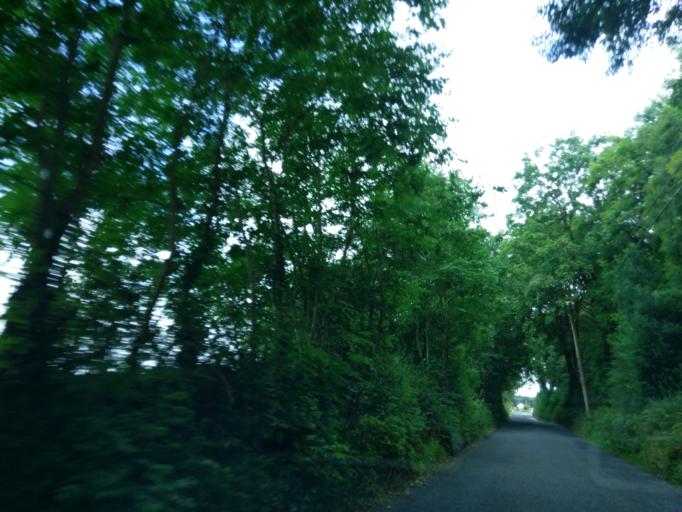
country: IE
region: Connaught
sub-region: County Galway
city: Athenry
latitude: 53.3266
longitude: -8.7860
